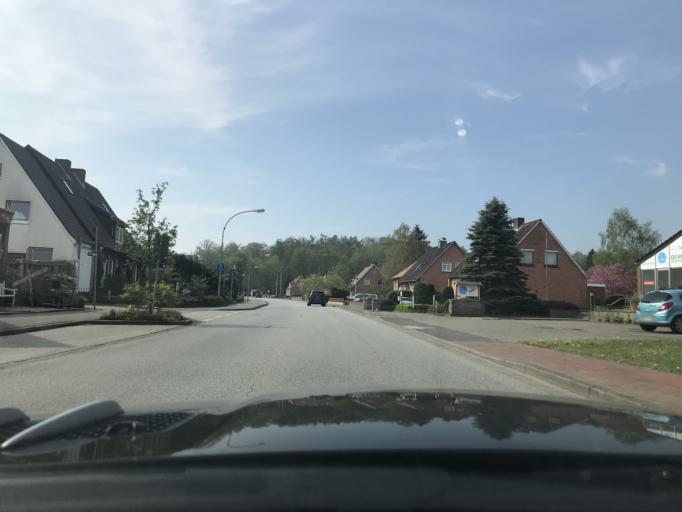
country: DE
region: Schleswig-Holstein
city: Riepsdorf
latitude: 54.1880
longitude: 10.9823
